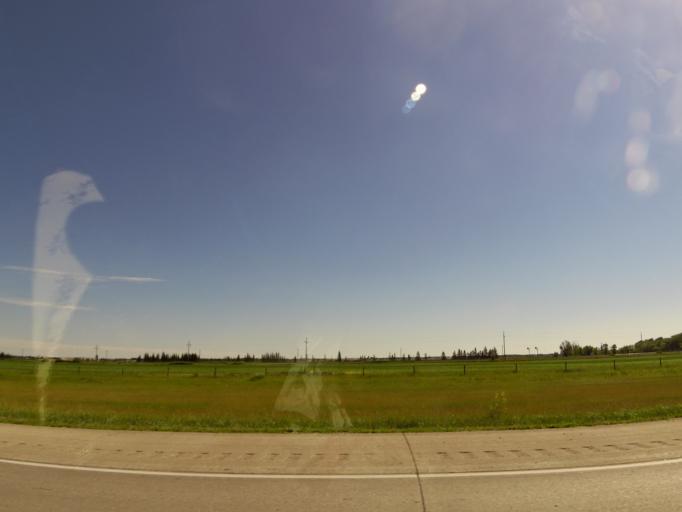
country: US
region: Minnesota
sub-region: Clay County
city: Oakport
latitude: 46.9222
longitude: -96.8432
